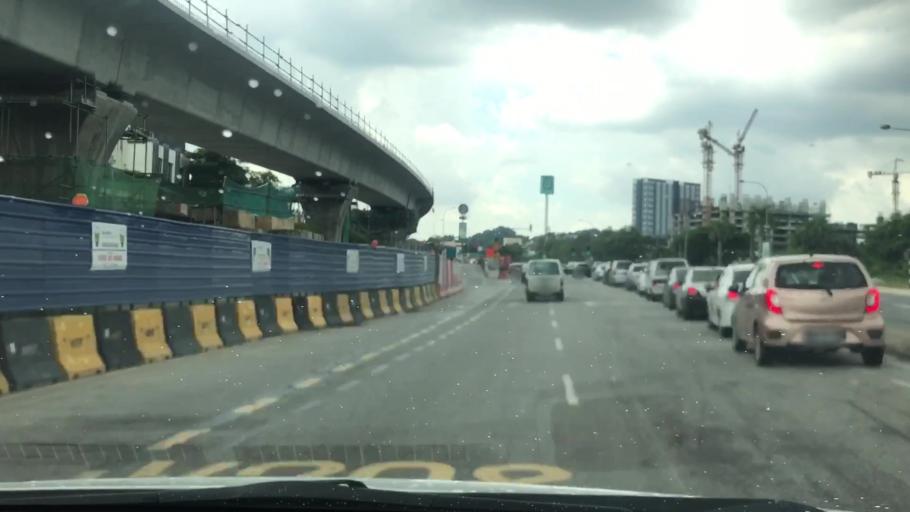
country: MY
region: Putrajaya
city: Putrajaya
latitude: 2.9955
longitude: 101.6792
